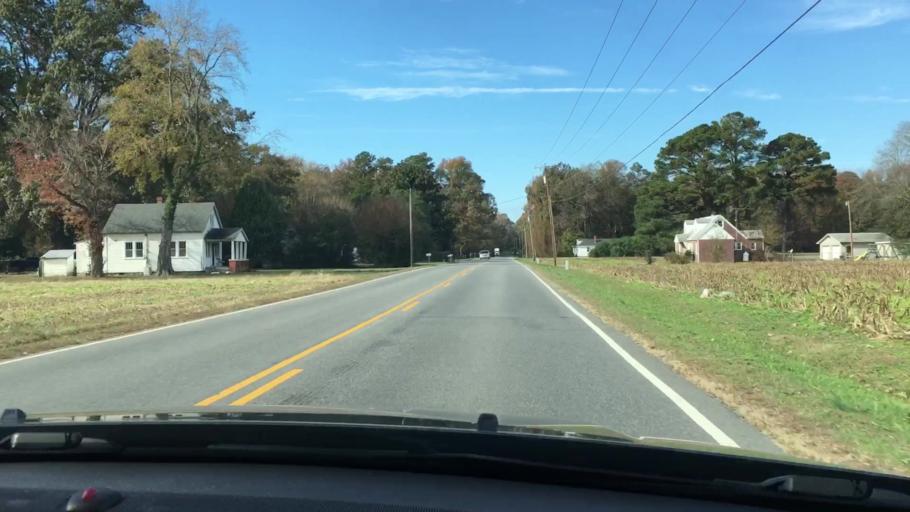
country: US
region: Virginia
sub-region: King William County
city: West Point
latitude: 37.5731
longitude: -76.8389
